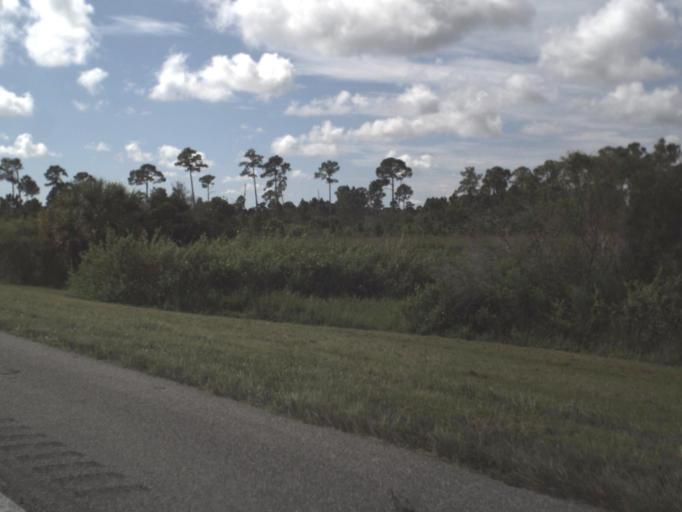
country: US
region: Florida
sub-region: Charlotte County
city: Port Charlotte
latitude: 27.0860
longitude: -82.1144
